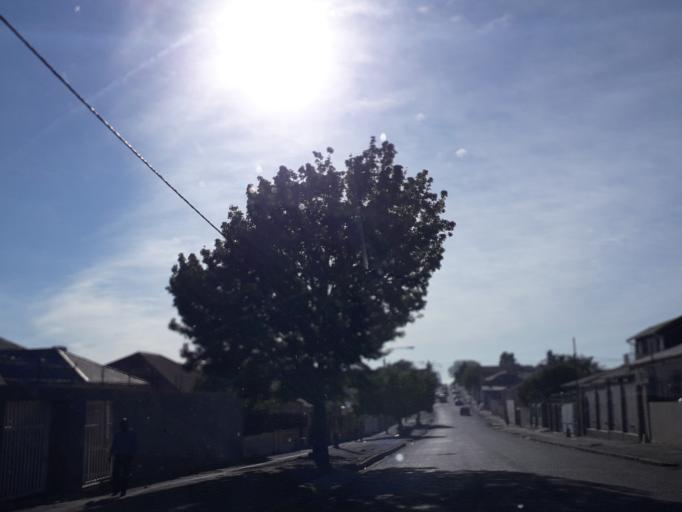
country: ZA
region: Gauteng
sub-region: City of Johannesburg Metropolitan Municipality
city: Johannesburg
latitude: -26.1910
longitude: 27.9945
